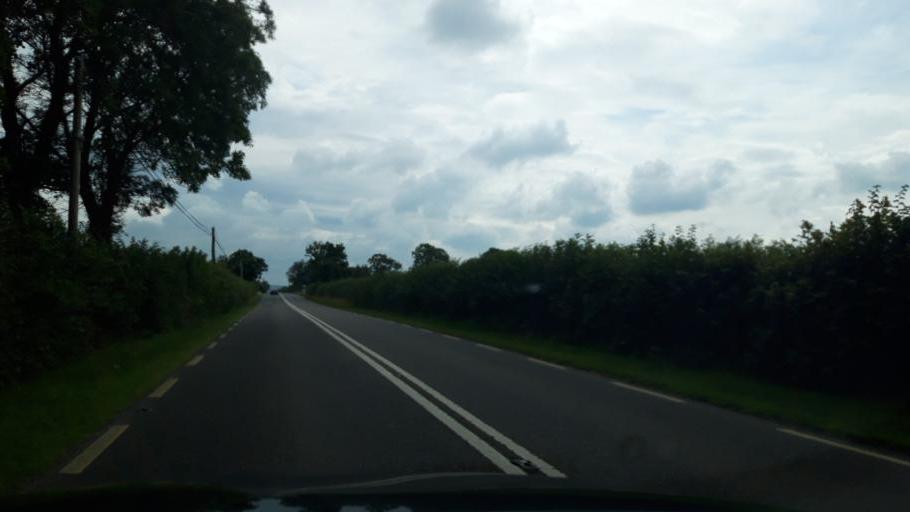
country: IE
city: Ballylinan
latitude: 52.9612
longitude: -7.0239
